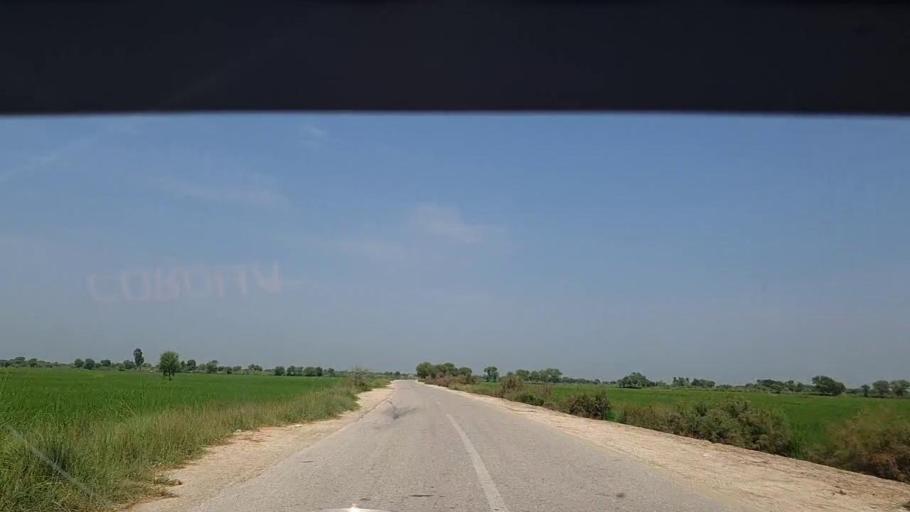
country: PK
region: Sindh
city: Thul
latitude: 28.1319
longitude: 68.8179
